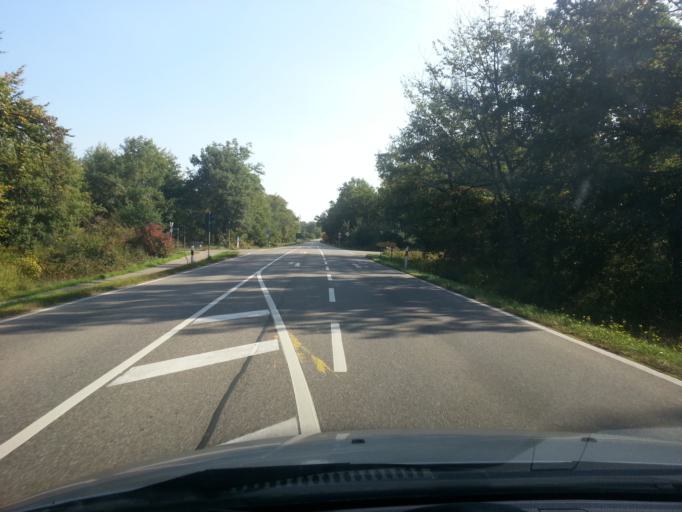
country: DE
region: Rheinland-Pfalz
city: Speyer
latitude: 49.3524
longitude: 8.4103
